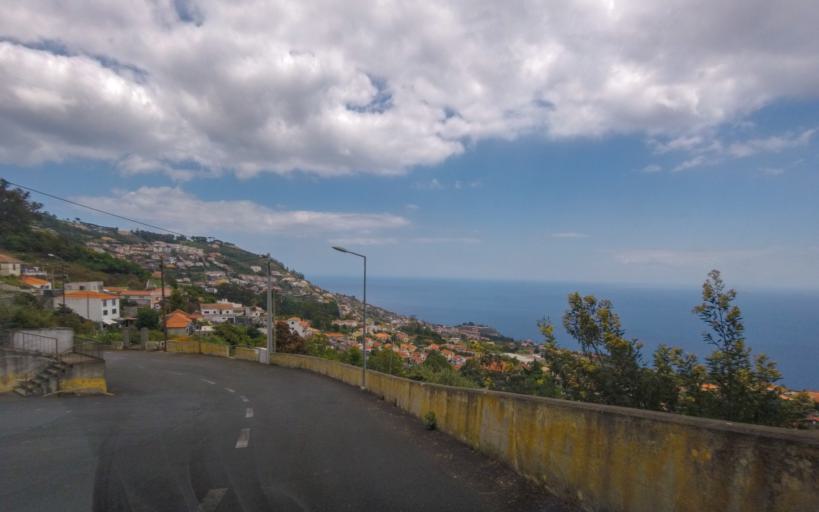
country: PT
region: Madeira
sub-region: Funchal
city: Nossa Senhora do Monte
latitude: 32.6625
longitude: -16.8834
